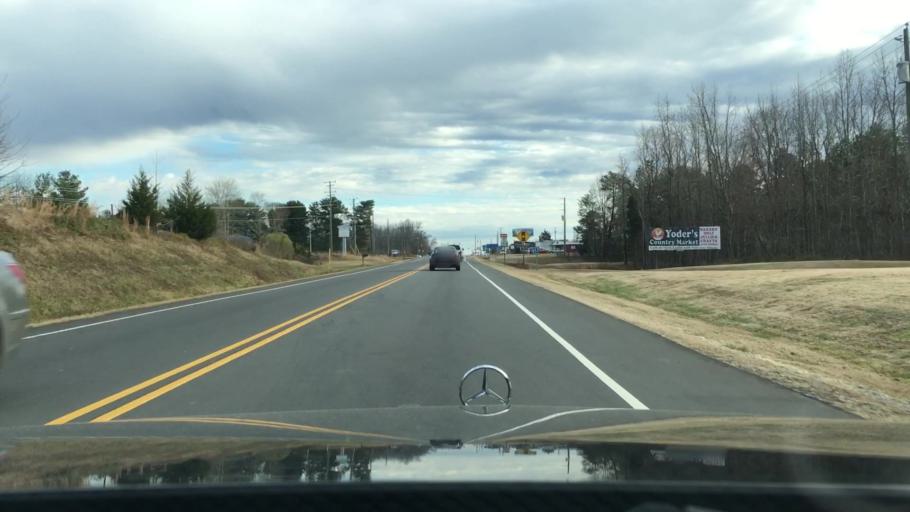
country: US
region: North Carolina
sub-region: Caswell County
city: Yanceyville
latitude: 36.4215
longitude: -79.3536
